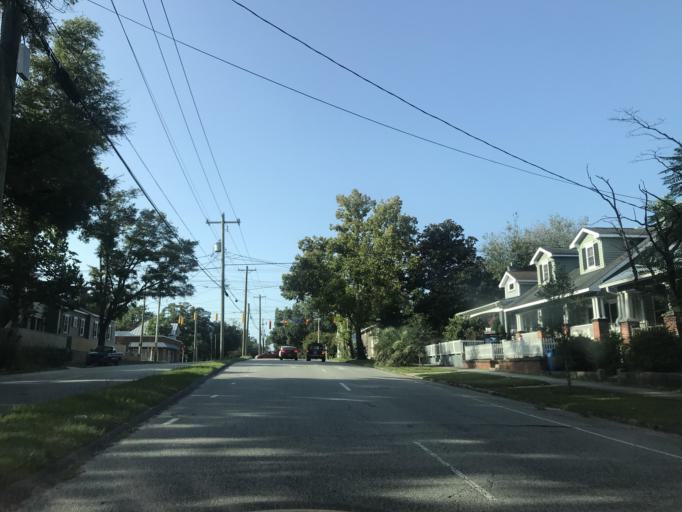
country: US
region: North Carolina
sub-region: New Hanover County
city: Wilmington
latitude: 34.2272
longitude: -77.9450
